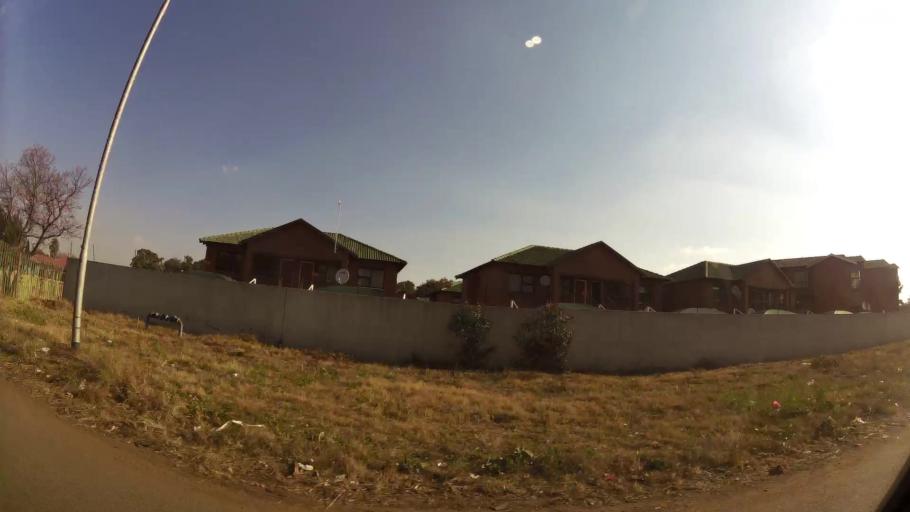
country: ZA
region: Gauteng
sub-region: Ekurhuleni Metropolitan Municipality
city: Brakpan
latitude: -26.2199
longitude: 28.3585
